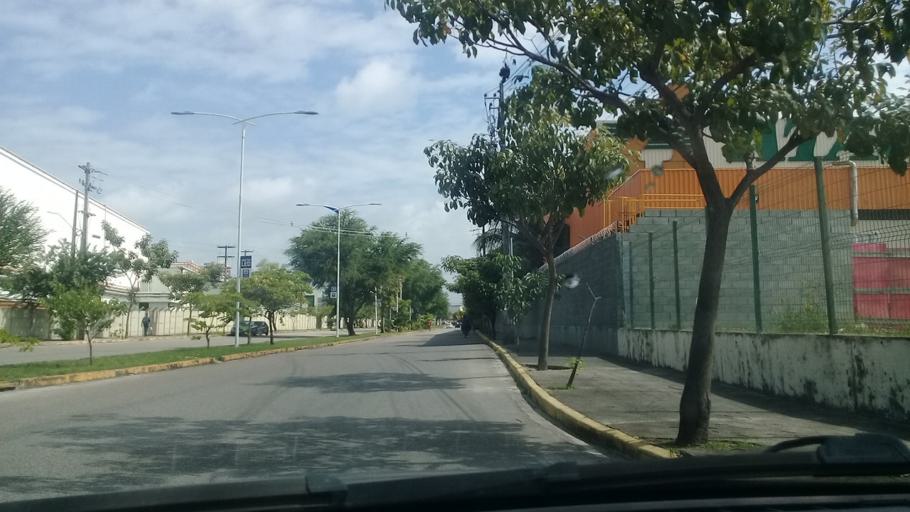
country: BR
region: Pernambuco
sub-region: Jaboatao Dos Guararapes
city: Jaboatao
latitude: -8.1658
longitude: -34.9196
